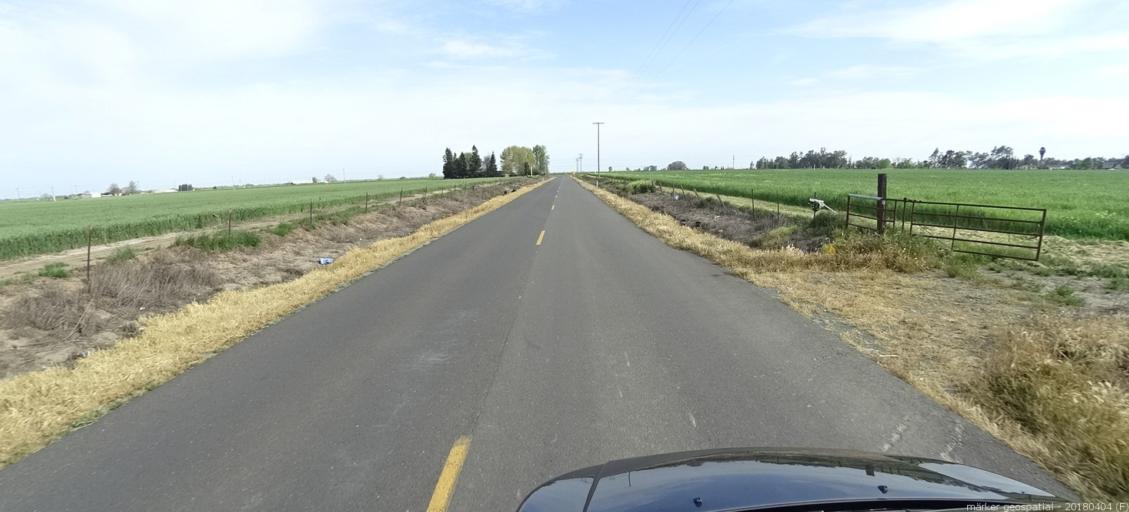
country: US
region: California
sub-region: Sacramento County
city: Herald
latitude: 38.3221
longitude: -121.3014
